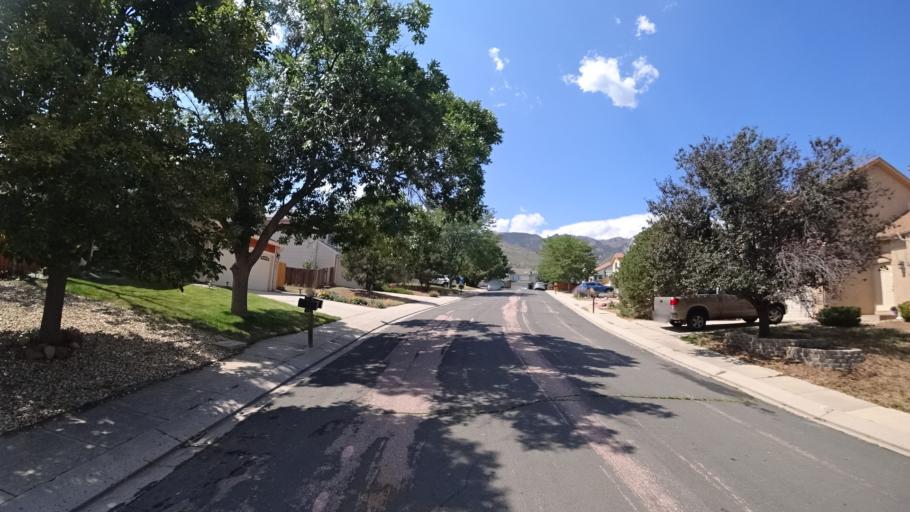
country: US
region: Colorado
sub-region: El Paso County
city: Air Force Academy
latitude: 38.9361
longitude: -104.8775
